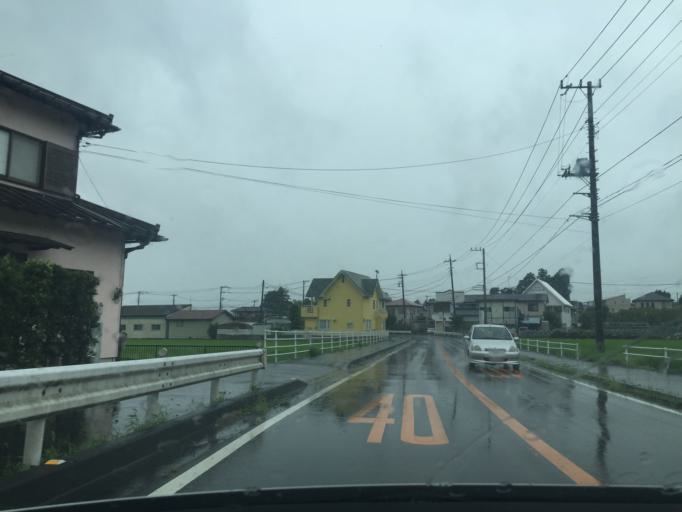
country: JP
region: Shizuoka
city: Mishima
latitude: 35.1700
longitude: 138.9190
